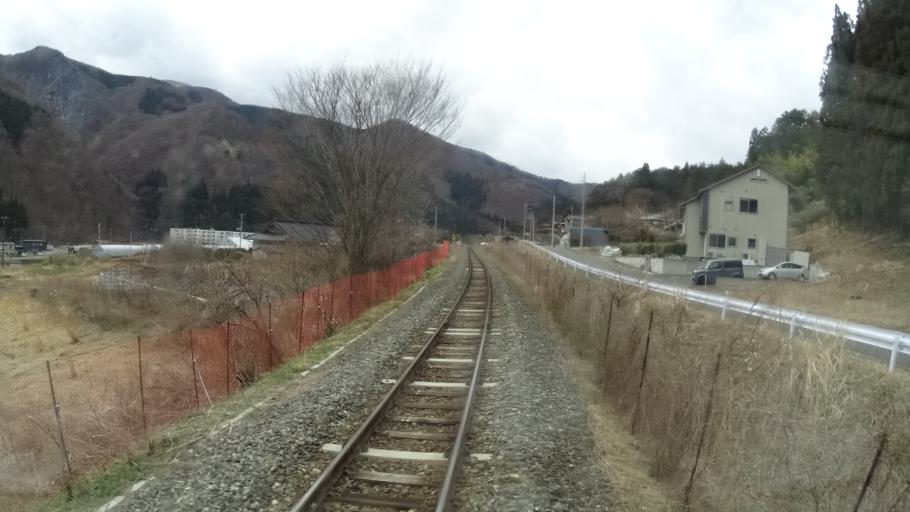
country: JP
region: Iwate
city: Kamaishi
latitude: 39.2524
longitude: 141.7668
